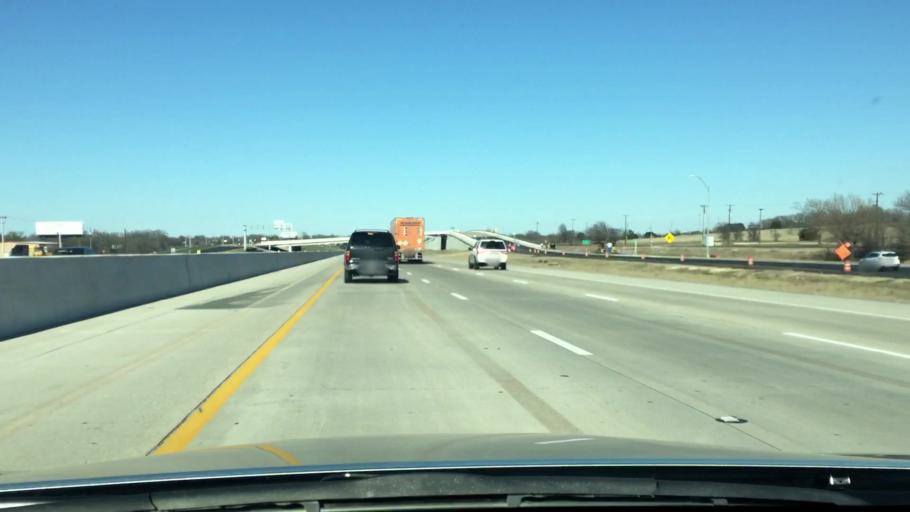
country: US
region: Texas
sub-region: Bell County
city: Troy
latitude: 31.1910
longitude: -97.3110
